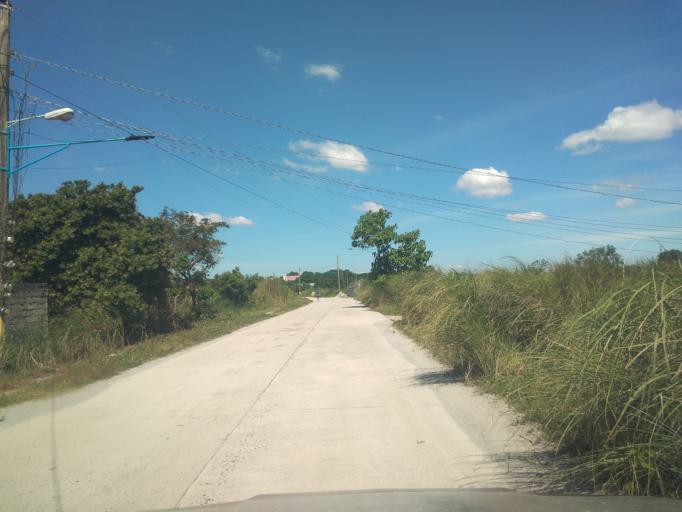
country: PH
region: Central Luzon
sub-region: Province of Pampanga
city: Balas
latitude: 15.0487
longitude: 120.6123
